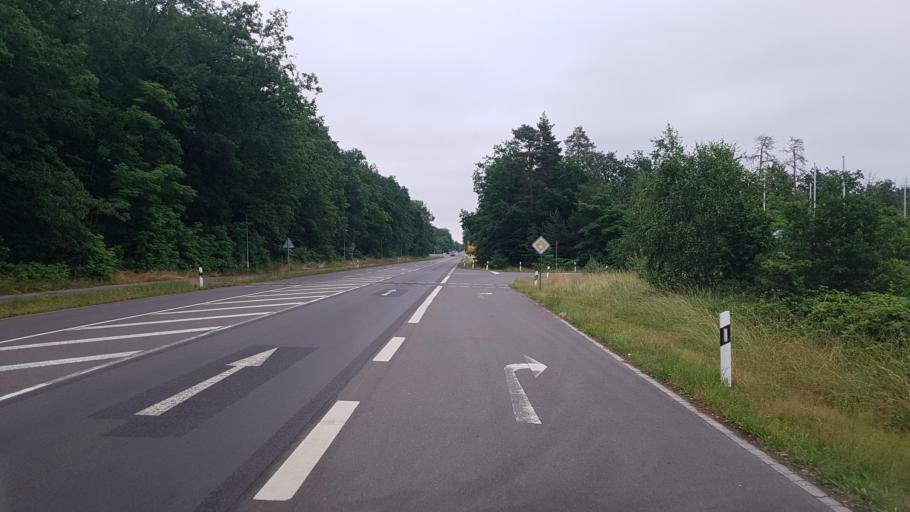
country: DE
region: Brandenburg
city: Senftenberg
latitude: 51.4969
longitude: 13.9579
